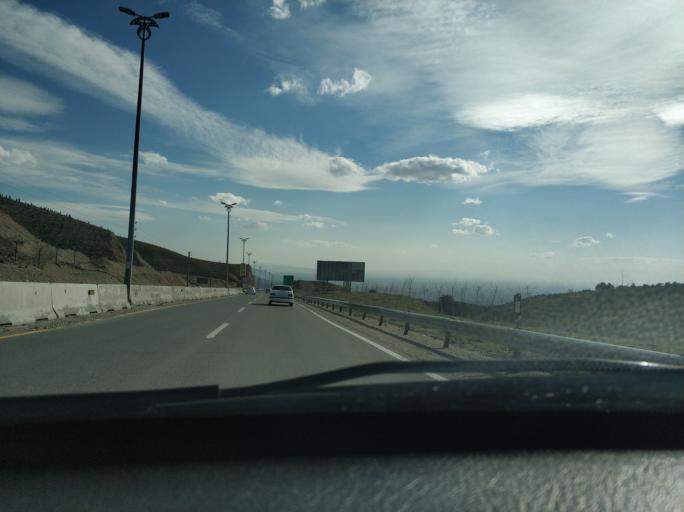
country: IR
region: Tehran
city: Tajrish
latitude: 35.7938
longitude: 51.5700
